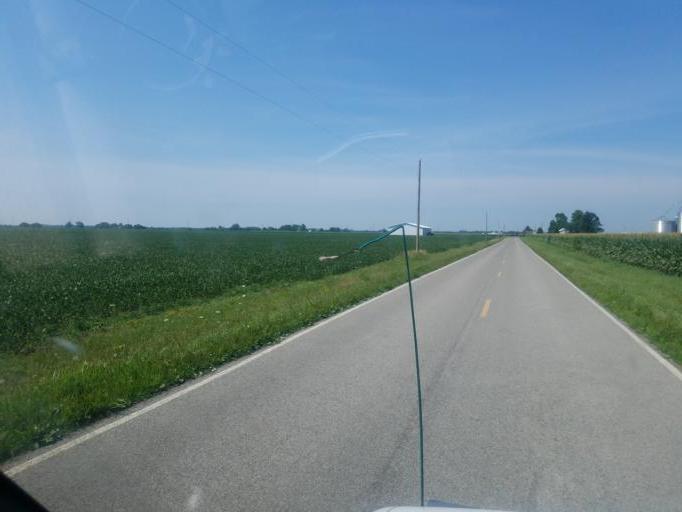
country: US
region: Ohio
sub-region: Champaign County
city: North Lewisburg
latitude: 40.2029
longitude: -83.5055
